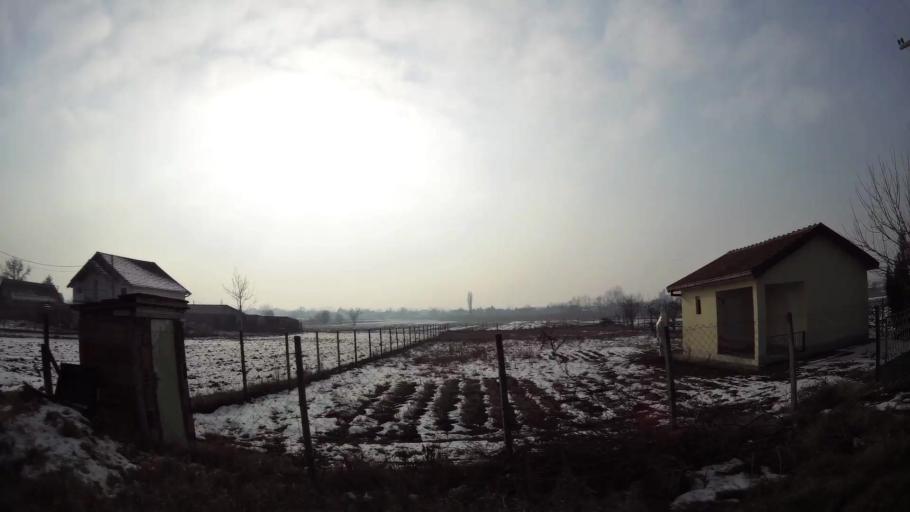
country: MK
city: Kadino
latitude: 41.9755
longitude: 21.6029
